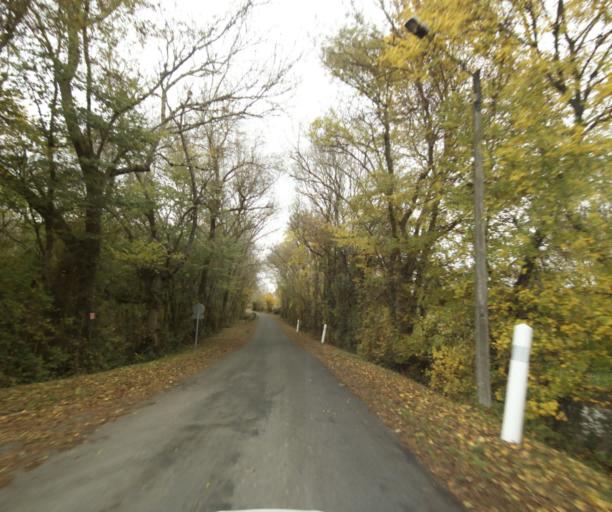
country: FR
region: Poitou-Charentes
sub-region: Departement de la Charente-Maritime
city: Saintes
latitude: 45.7600
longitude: -0.6270
